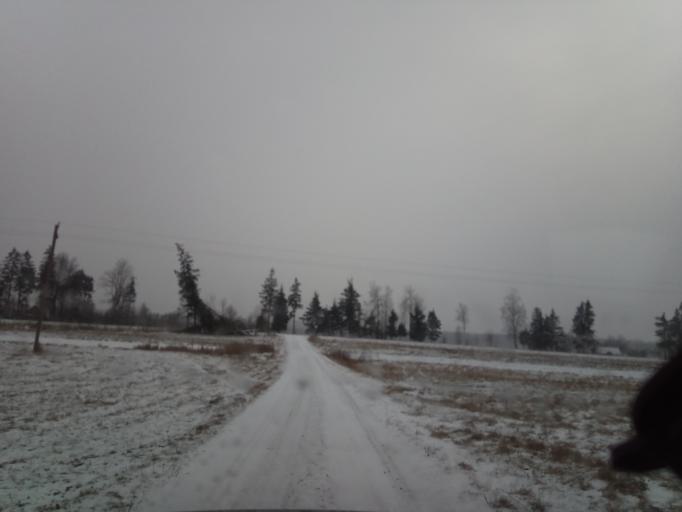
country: LT
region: Utenos apskritis
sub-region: Anyksciai
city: Anyksciai
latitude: 55.4024
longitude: 25.1699
